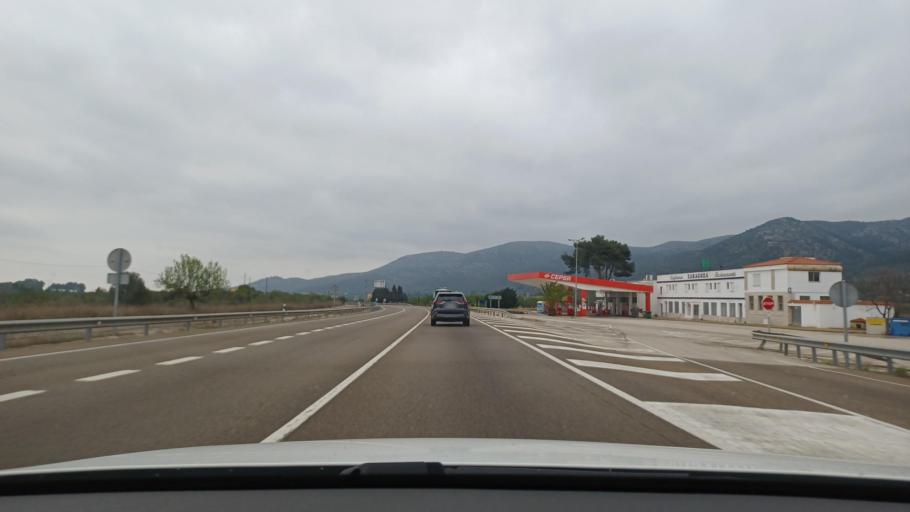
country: ES
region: Valencia
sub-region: Provincia de Castello
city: Santa Magdalena de Pulpis
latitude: 40.3599
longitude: 0.3020
